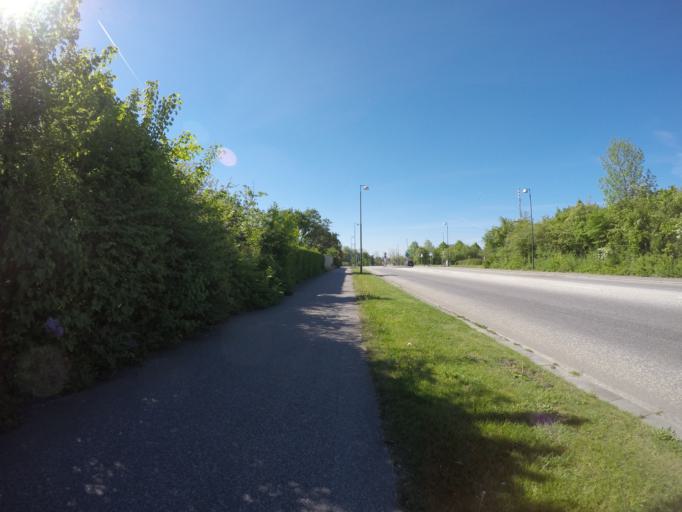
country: SE
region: Skane
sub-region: Burlovs Kommun
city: Arloev
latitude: 55.5766
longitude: 13.0611
